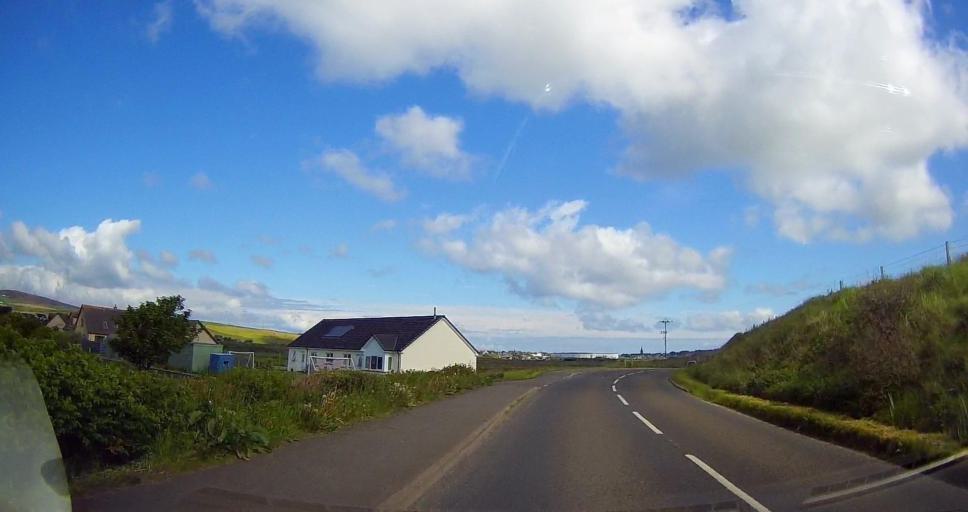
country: GB
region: Scotland
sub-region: Orkney Islands
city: Orkney
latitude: 58.9613
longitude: -2.9684
